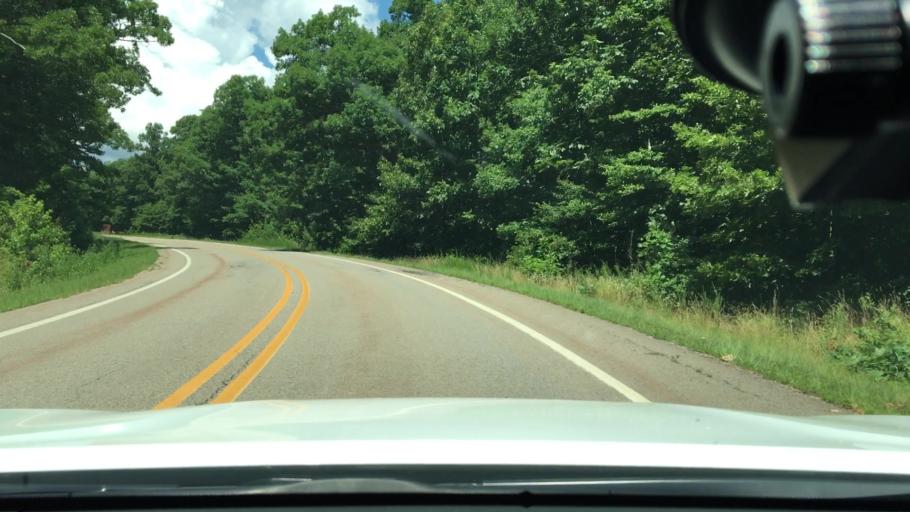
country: US
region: Arkansas
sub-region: Logan County
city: Paris
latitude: 35.1704
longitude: -93.6427
